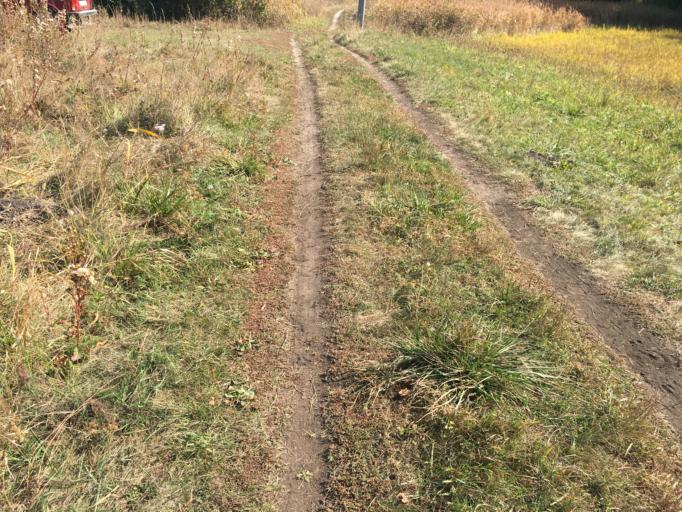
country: RU
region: Saratov
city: Svetlyy
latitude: 51.6551
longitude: 45.7092
